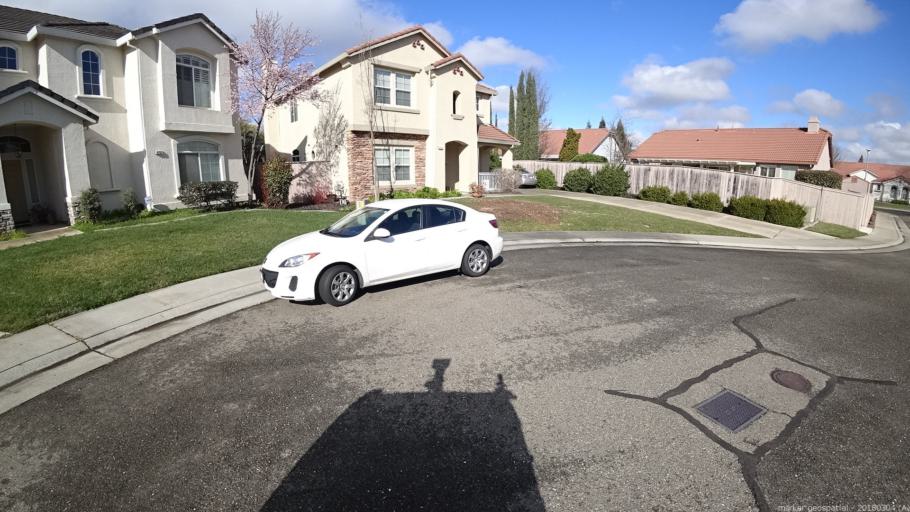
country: US
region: California
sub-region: Sacramento County
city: Vineyard
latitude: 38.4579
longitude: -121.3199
